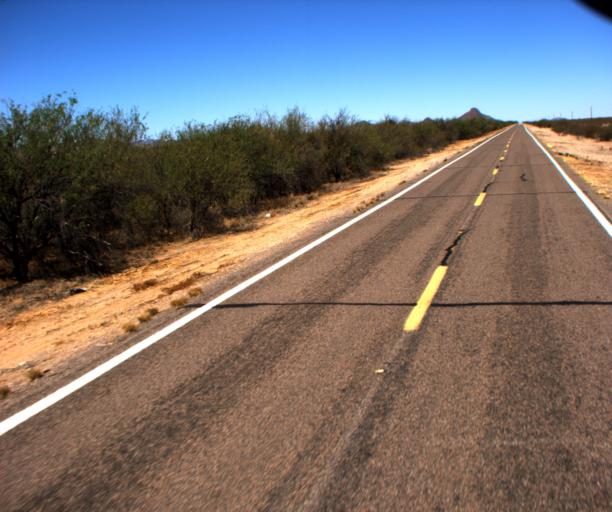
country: US
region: Arizona
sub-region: Pima County
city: Ajo
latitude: 32.1987
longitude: -112.4825
